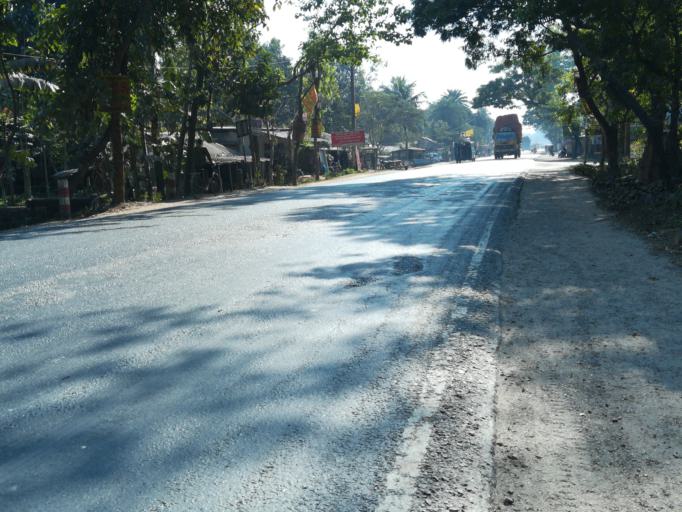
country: BD
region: Rangpur Division
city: Rangpur
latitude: 25.5747
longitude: 89.2745
